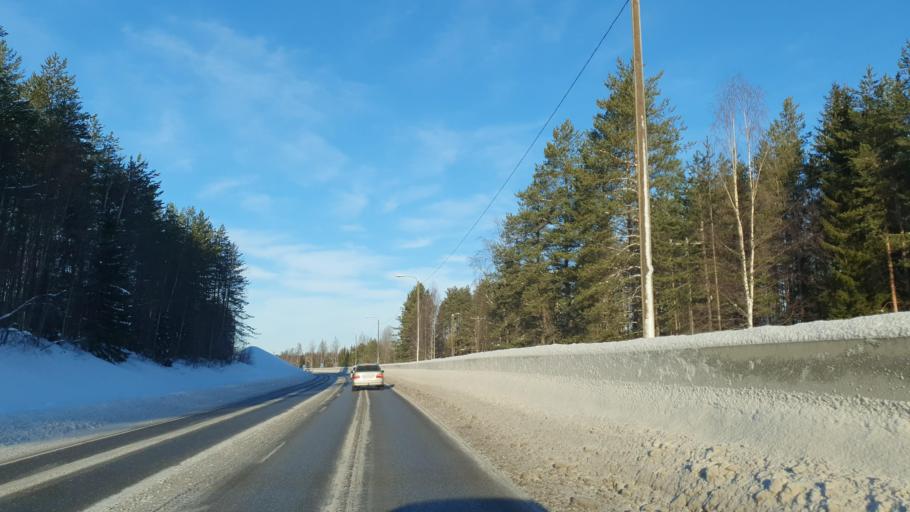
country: FI
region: Northern Ostrobothnia
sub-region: Oulu
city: Kempele
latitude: 64.9680
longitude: 25.6260
